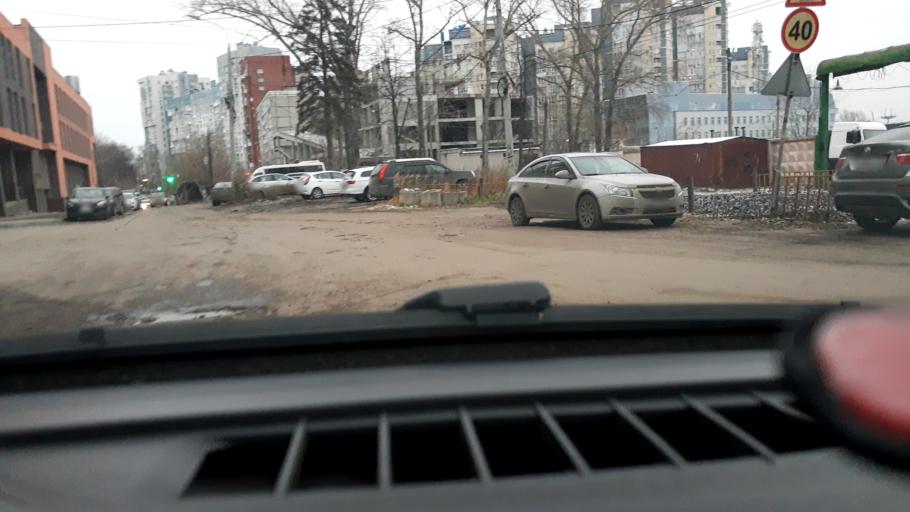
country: RU
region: Nizjnij Novgorod
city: Nizhniy Novgorod
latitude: 56.3067
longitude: 44.0012
